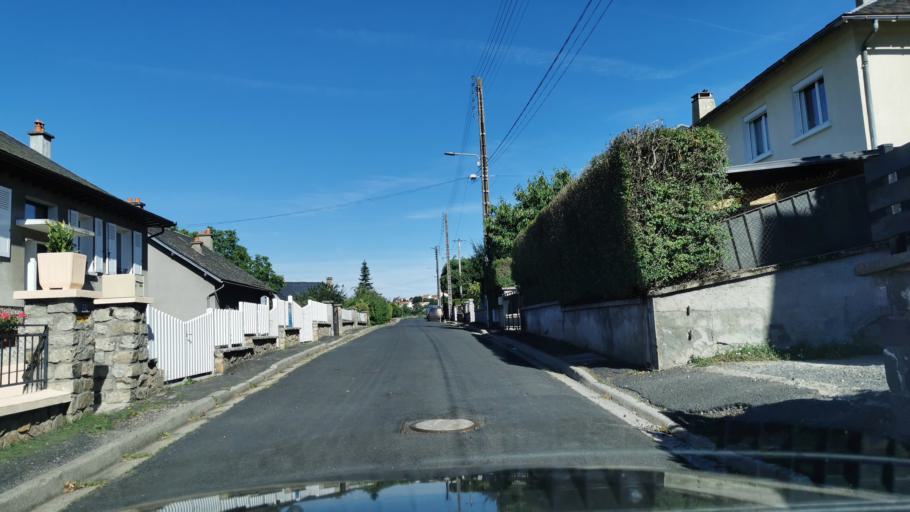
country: FR
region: Auvergne
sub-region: Departement du Cantal
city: Saint-Flour
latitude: 45.0378
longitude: 3.1060
